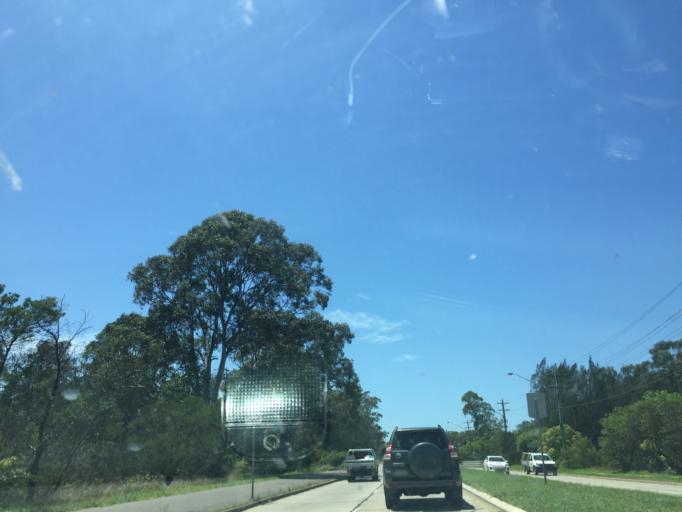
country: AU
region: New South Wales
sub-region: Blacktown
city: Glendenning
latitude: -33.7409
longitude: 150.8646
